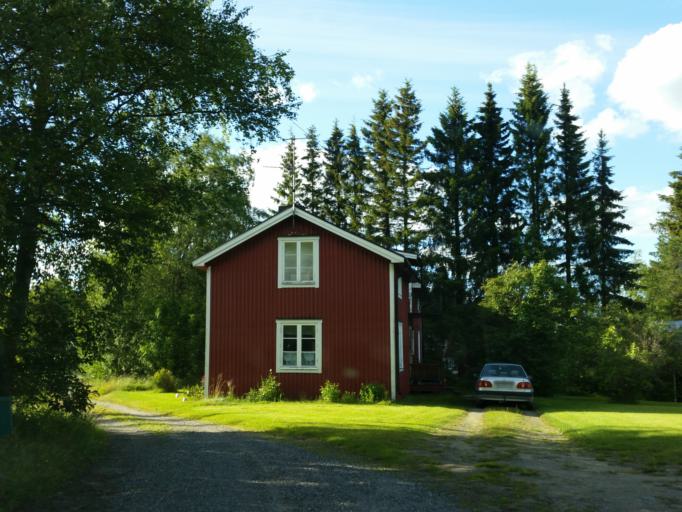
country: SE
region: Vaesterbotten
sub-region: Robertsfors Kommun
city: Robertsfors
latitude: 64.0399
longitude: 20.8617
